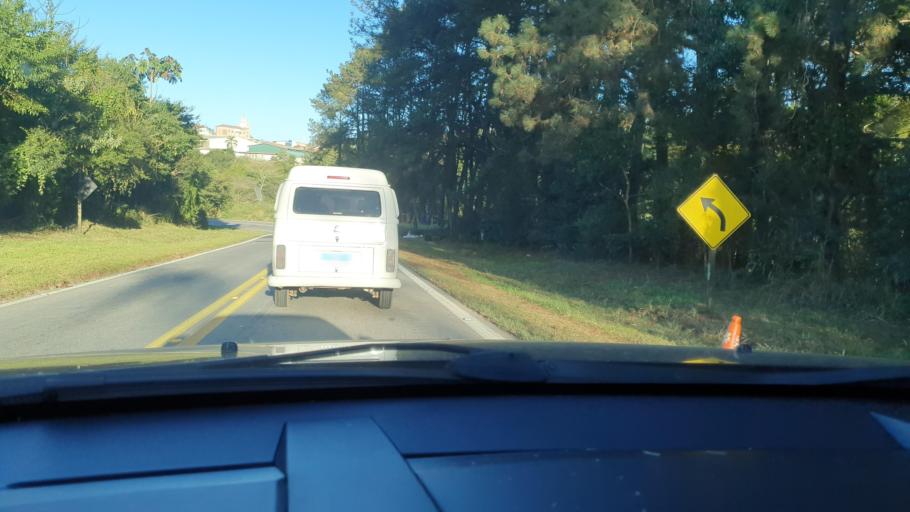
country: BR
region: Sao Paulo
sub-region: Piedade
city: Piedade
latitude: -23.7118
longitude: -47.3982
